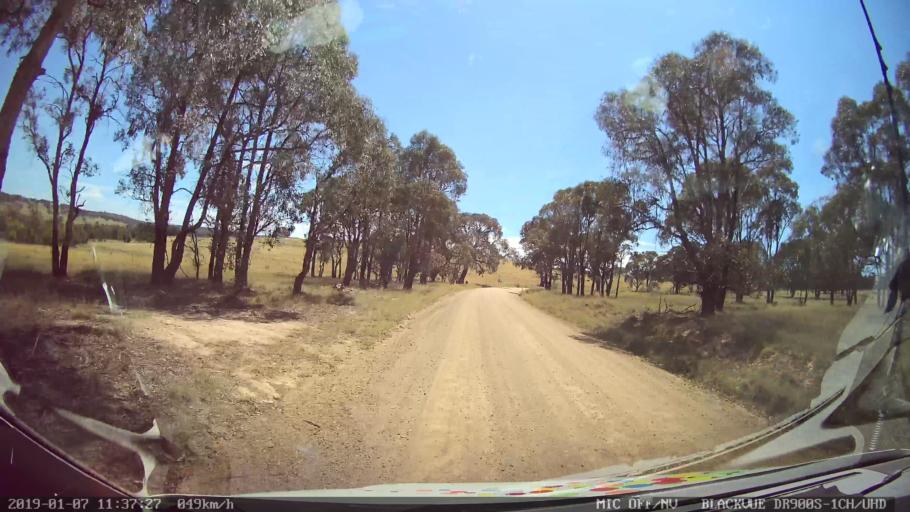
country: AU
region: New South Wales
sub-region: Armidale Dumaresq
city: Armidale
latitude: -30.3708
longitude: 151.5656
